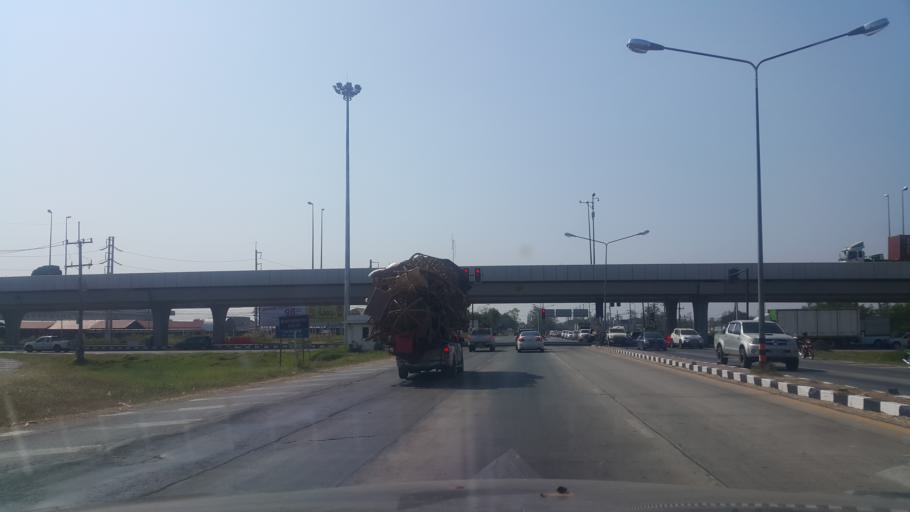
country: TH
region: Nakhon Ratchasima
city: Pak Thong Chai
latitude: 14.7595
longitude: 102.0383
